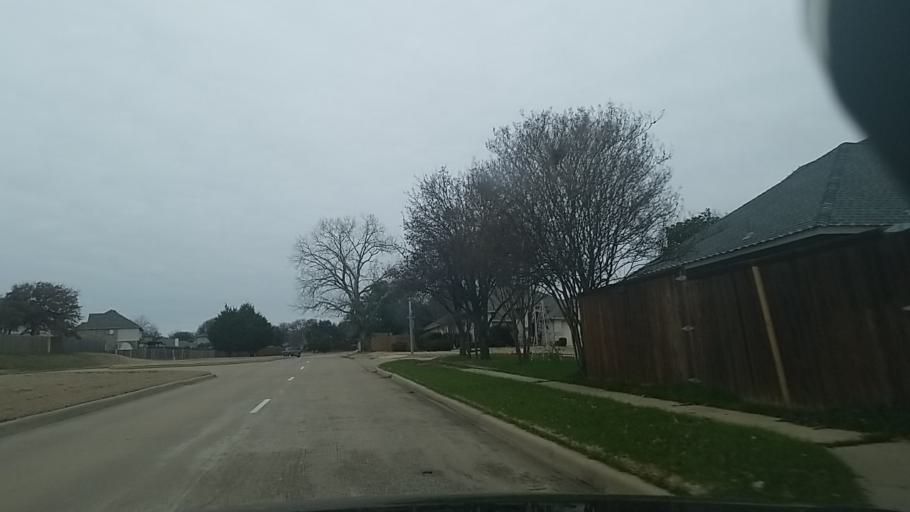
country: US
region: Texas
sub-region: Denton County
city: Corinth
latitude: 33.1385
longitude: -97.0772
